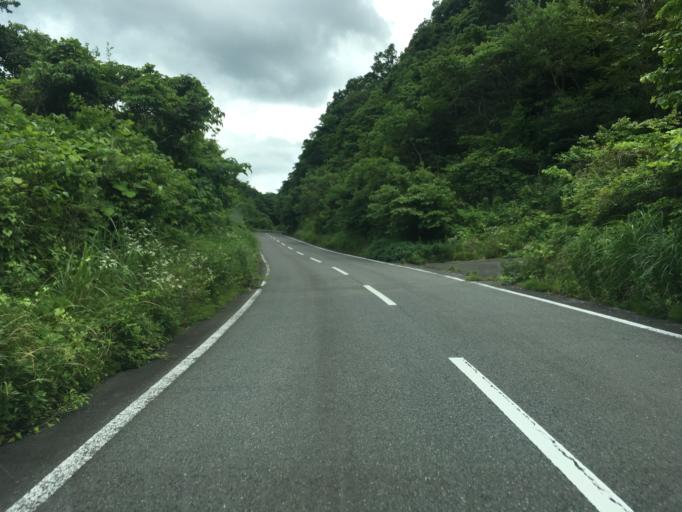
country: JP
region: Miyagi
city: Marumori
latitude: 37.7066
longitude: 140.8775
